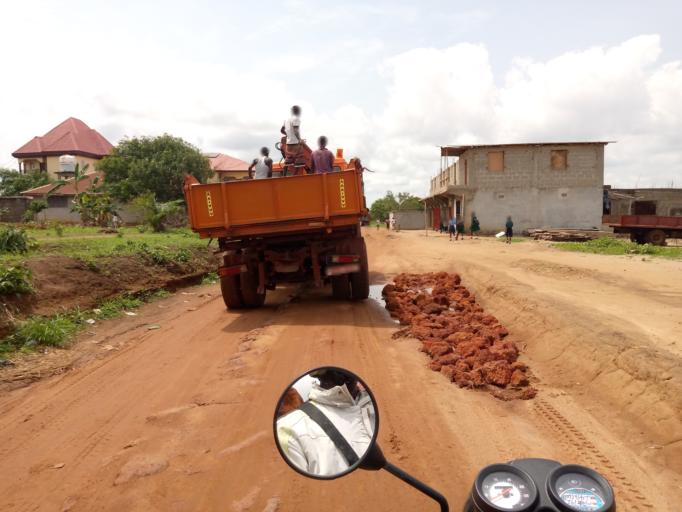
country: SL
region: Western Area
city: Waterloo
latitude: 8.3597
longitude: -13.0721
